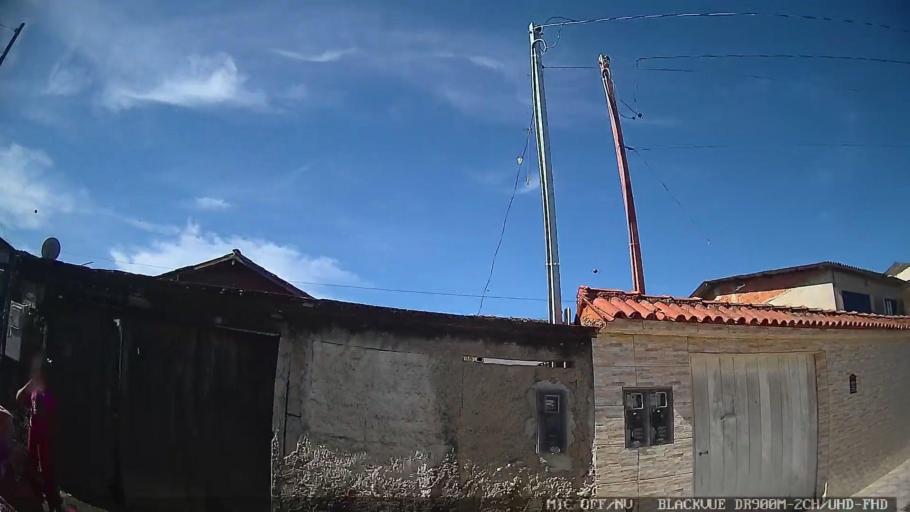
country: BR
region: Sao Paulo
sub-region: Santos
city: Santos
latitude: -23.9456
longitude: -46.2838
